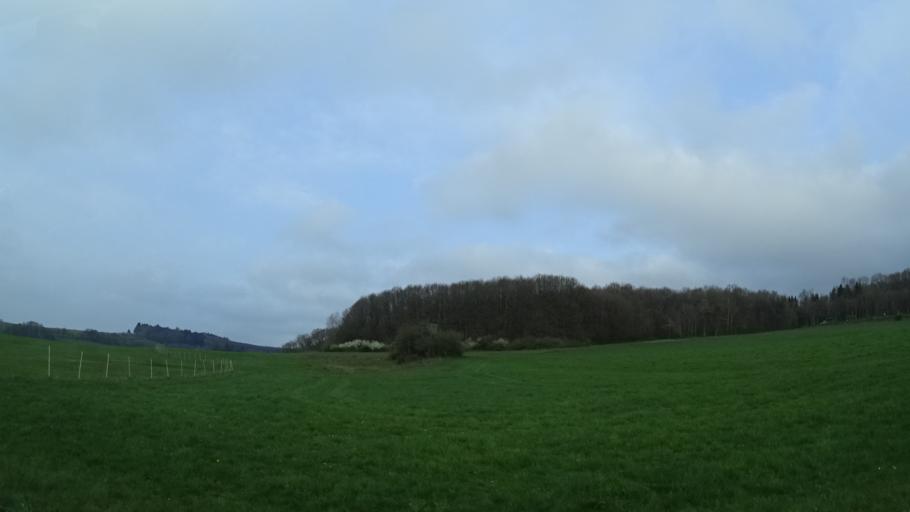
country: DE
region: Rheinland-Pfalz
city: Leisel
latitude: 49.7232
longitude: 7.1993
